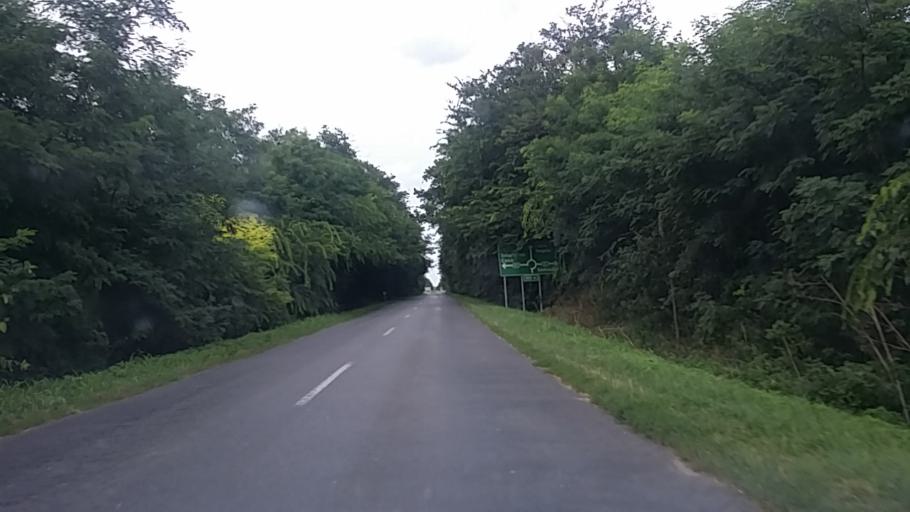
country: HU
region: Tolna
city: Tengelic
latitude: 46.5310
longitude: 18.6508
